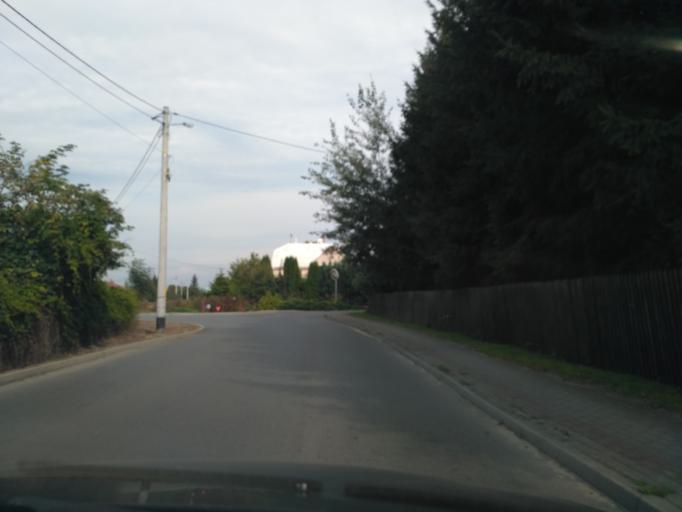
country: PL
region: Subcarpathian Voivodeship
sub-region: Powiat rzeszowski
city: Swilcza
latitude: 50.0799
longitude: 21.9019
